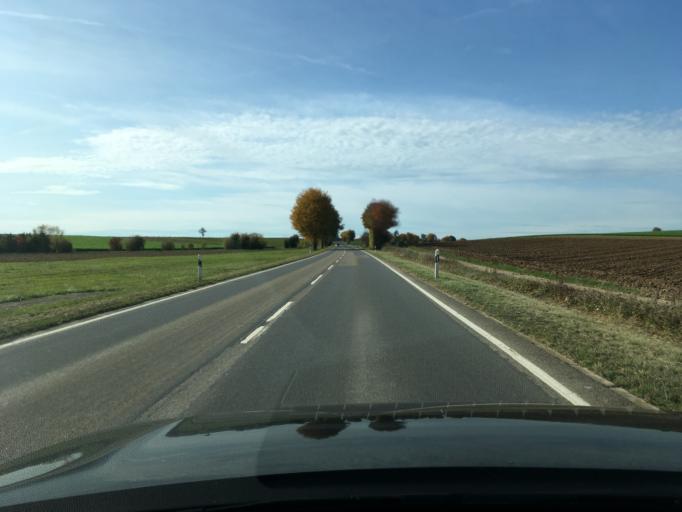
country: DE
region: Baden-Wuerttemberg
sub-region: Regierungsbezirk Stuttgart
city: Bad Rappenau
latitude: 49.2340
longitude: 9.0736
